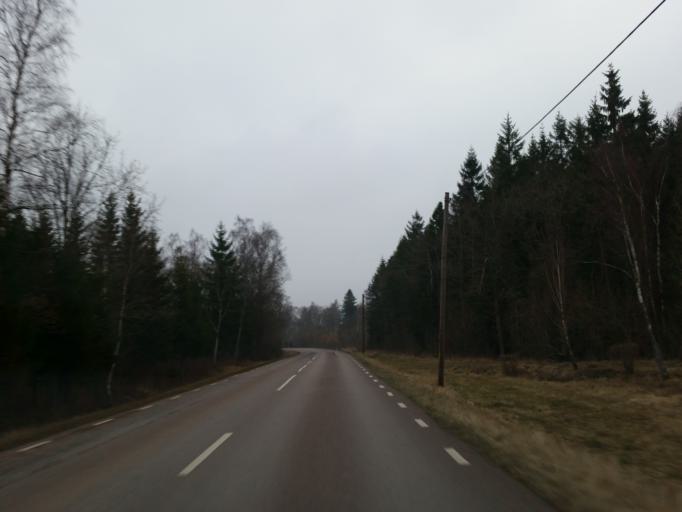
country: SE
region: Kalmar
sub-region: Morbylanga Kommun
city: Sodra Sandby
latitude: 56.6265
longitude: 16.5994
